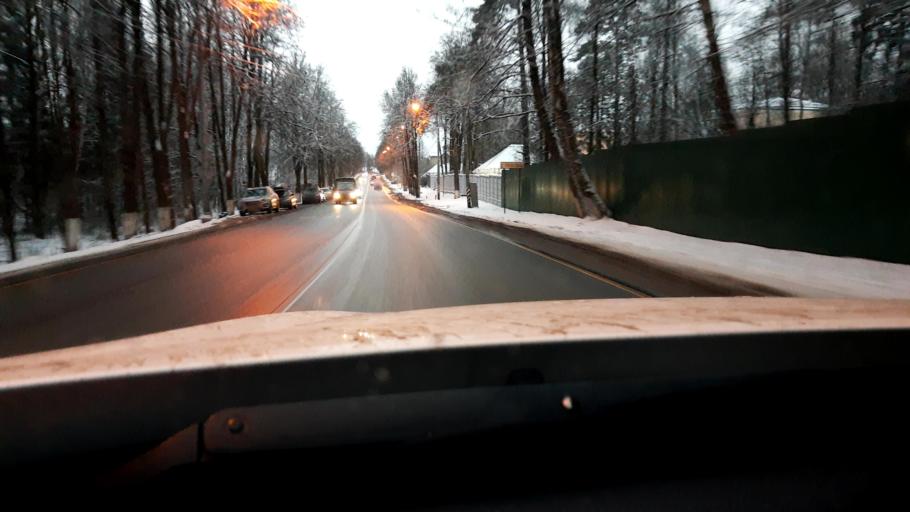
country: RU
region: Moskovskaya
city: Barvikha
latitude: 55.7789
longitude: 37.2563
